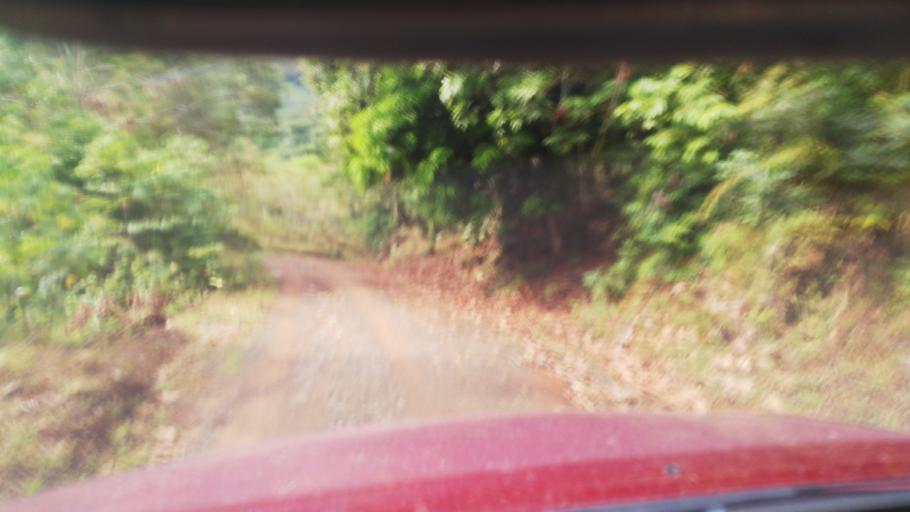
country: CO
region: Risaralda
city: La Virginia
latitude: 4.8758
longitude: -75.9417
